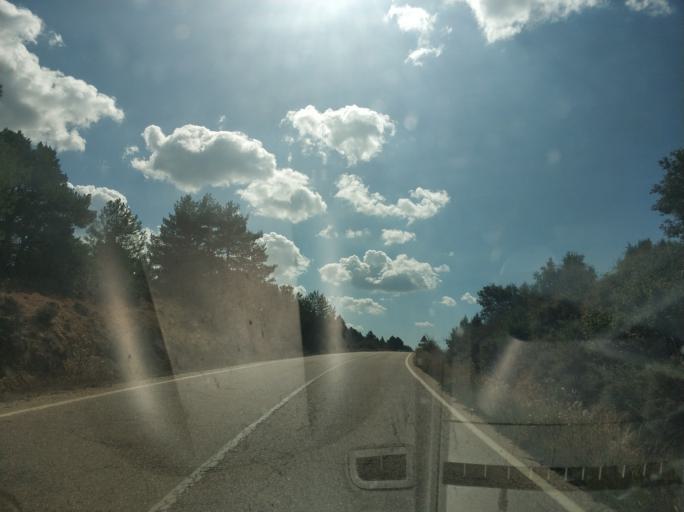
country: ES
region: Castille and Leon
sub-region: Provincia de Soria
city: Casarejos
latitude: 41.7788
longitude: -3.0267
